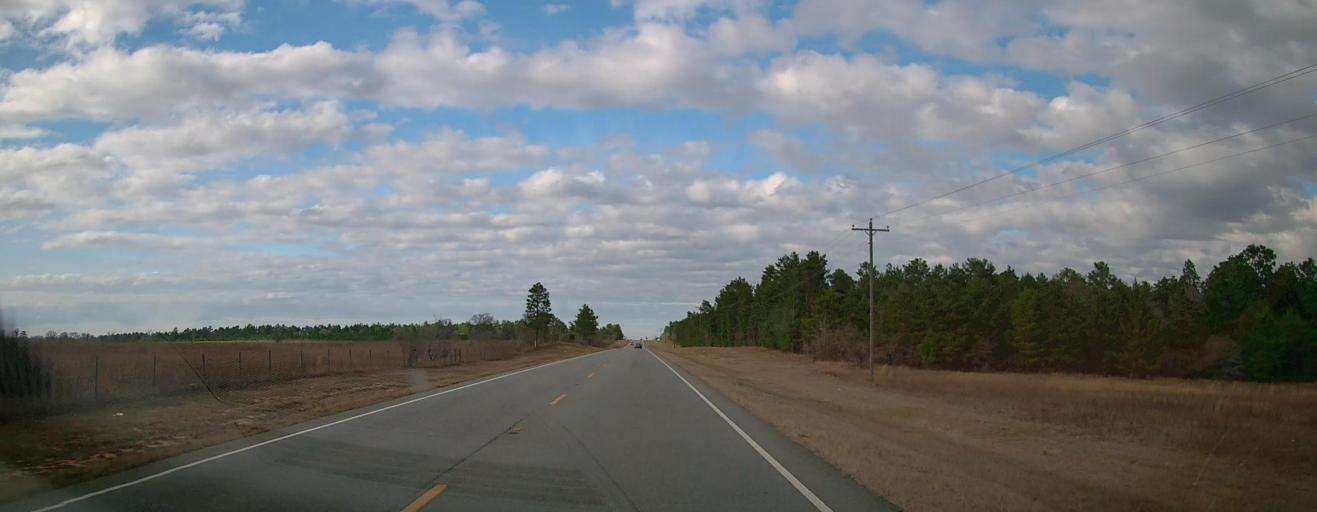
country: US
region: Georgia
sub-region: Marion County
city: Buena Vista
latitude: 32.4725
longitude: -84.5422
